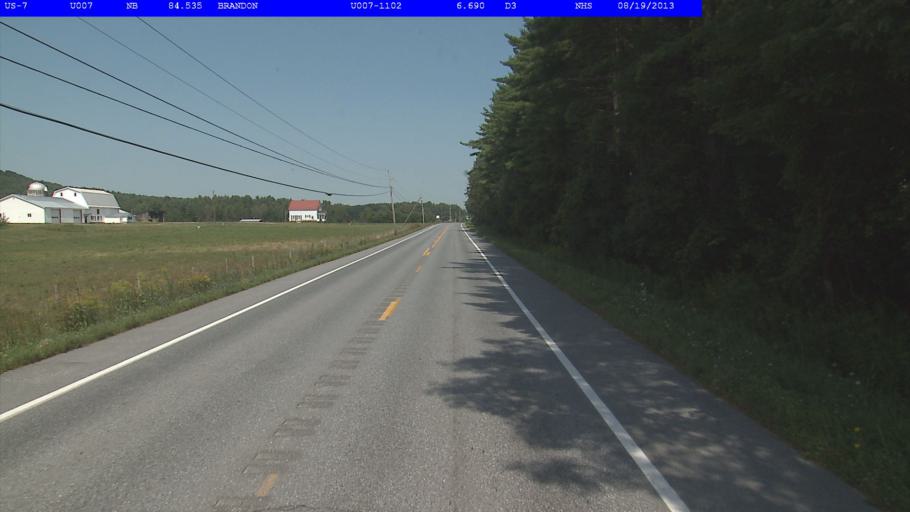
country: US
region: Vermont
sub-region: Rutland County
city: Brandon
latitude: 43.8326
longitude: -73.1056
